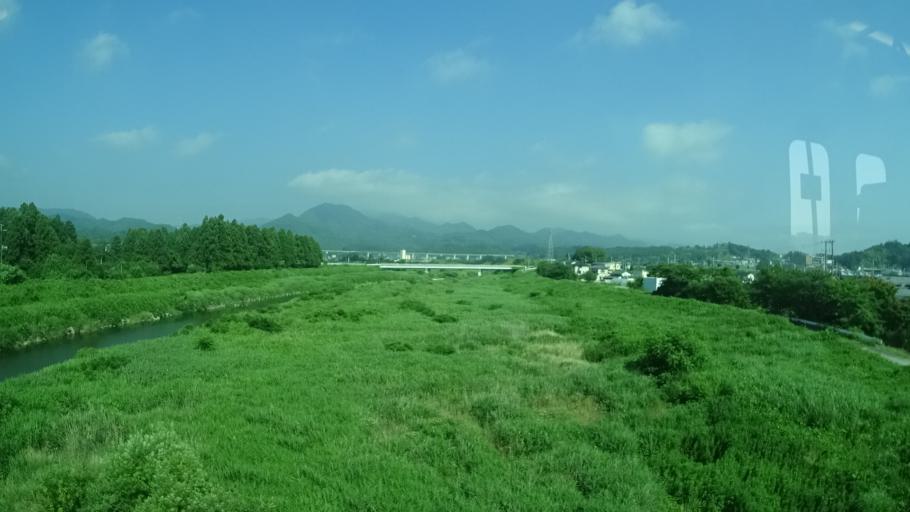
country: JP
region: Fukushima
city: Namie
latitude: 37.2729
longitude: 140.9974
